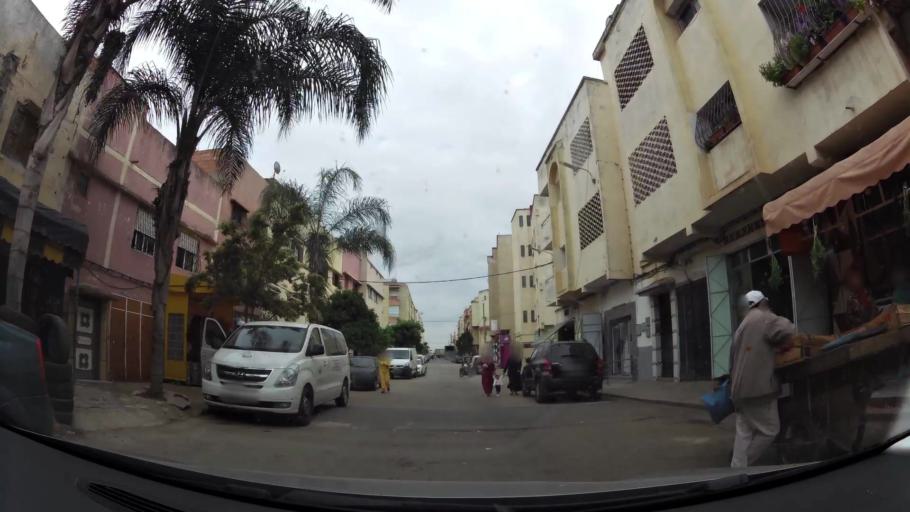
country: MA
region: Rabat-Sale-Zemmour-Zaer
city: Sale
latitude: 34.0319
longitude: -6.8001
